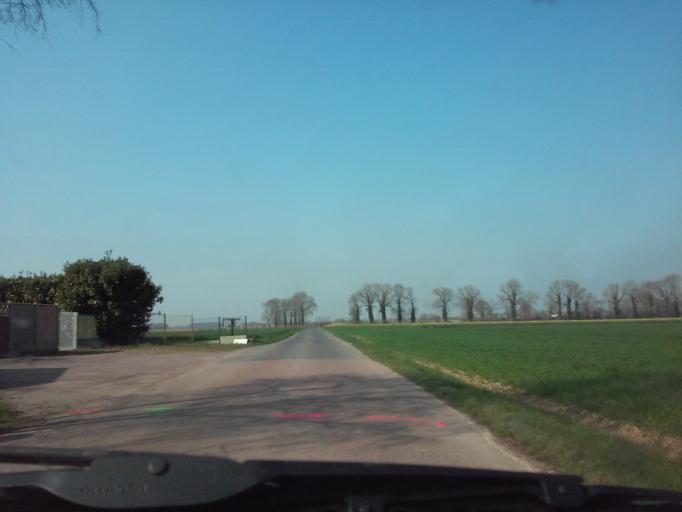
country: FR
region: Lower Normandy
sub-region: Departement du Calvados
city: Cheux
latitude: 49.1973
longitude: -0.5463
